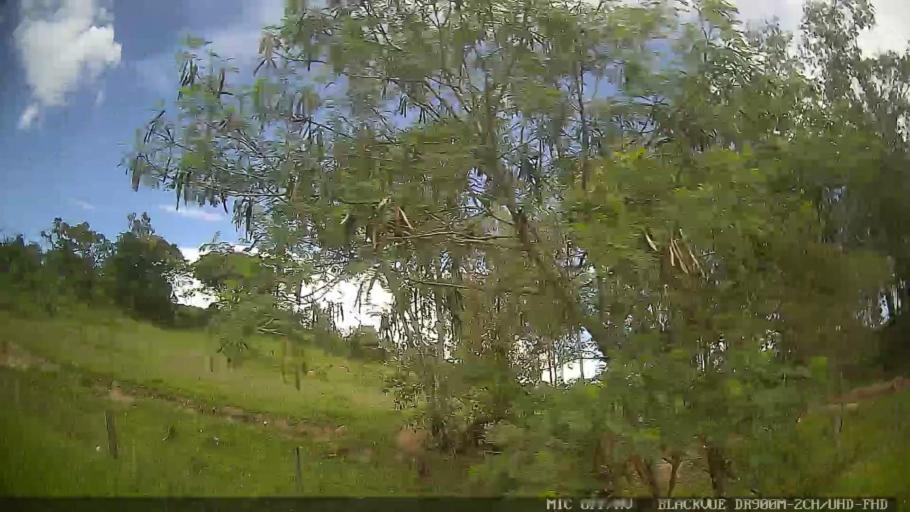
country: BR
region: Sao Paulo
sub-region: Conchas
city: Conchas
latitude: -22.9977
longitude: -47.9997
